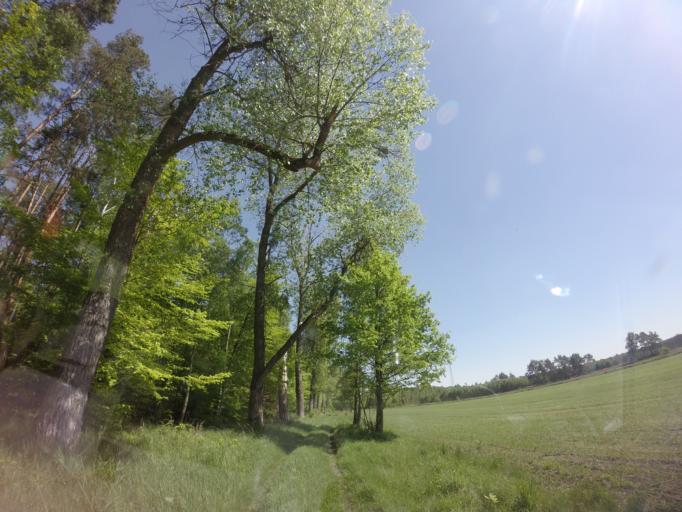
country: PL
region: West Pomeranian Voivodeship
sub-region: Powiat choszczenski
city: Pelczyce
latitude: 52.9451
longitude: 15.3437
